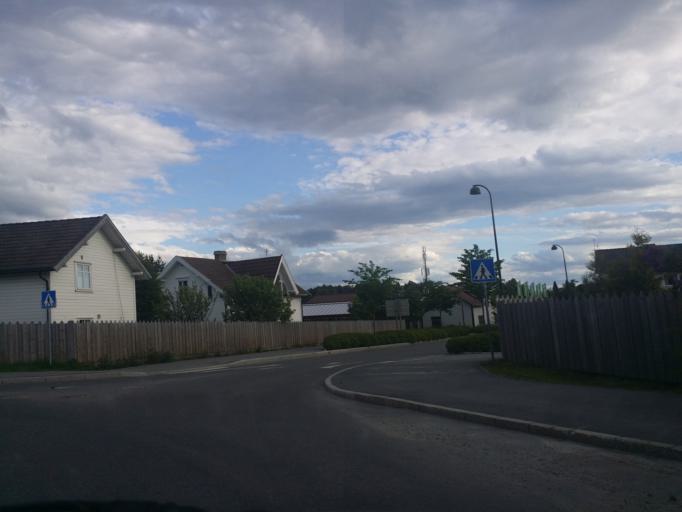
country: NO
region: Hedmark
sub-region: Ringsaker
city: Brumunddal
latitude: 60.8862
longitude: 10.9485
